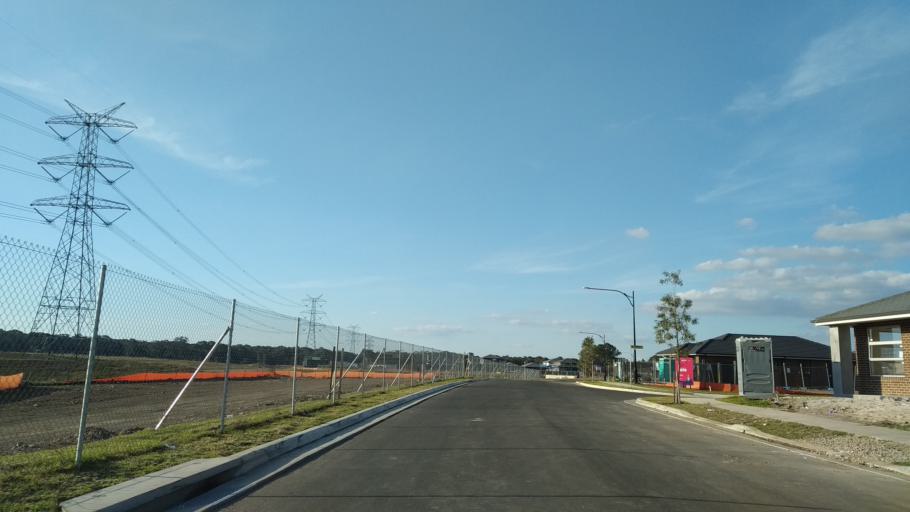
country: AU
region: New South Wales
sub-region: Penrith Municipality
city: Werrington County
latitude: -33.7318
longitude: 150.7536
